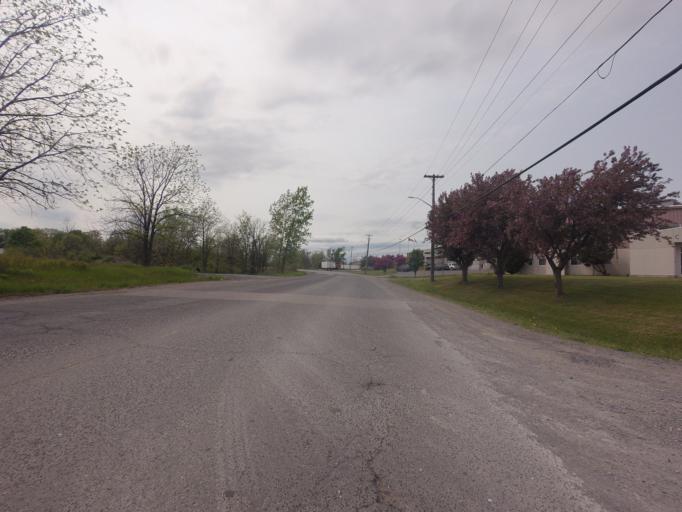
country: CA
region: Ontario
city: Kingston
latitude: 44.2685
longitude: -76.5113
